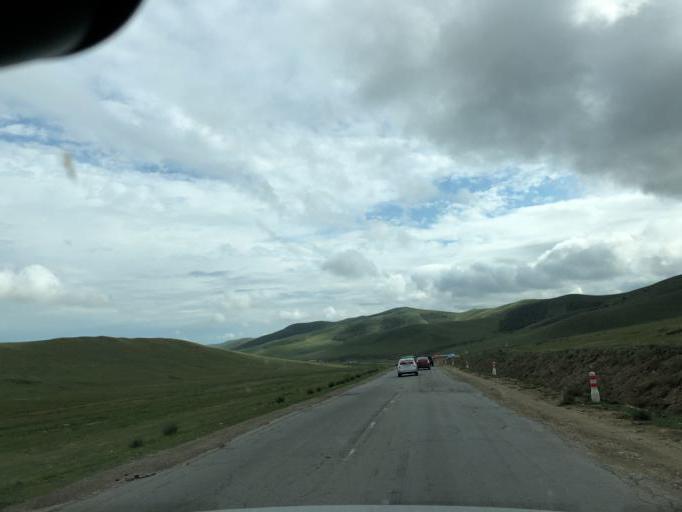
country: MN
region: Central Aimak
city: Ihsueuej
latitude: 48.1202
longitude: 106.4359
